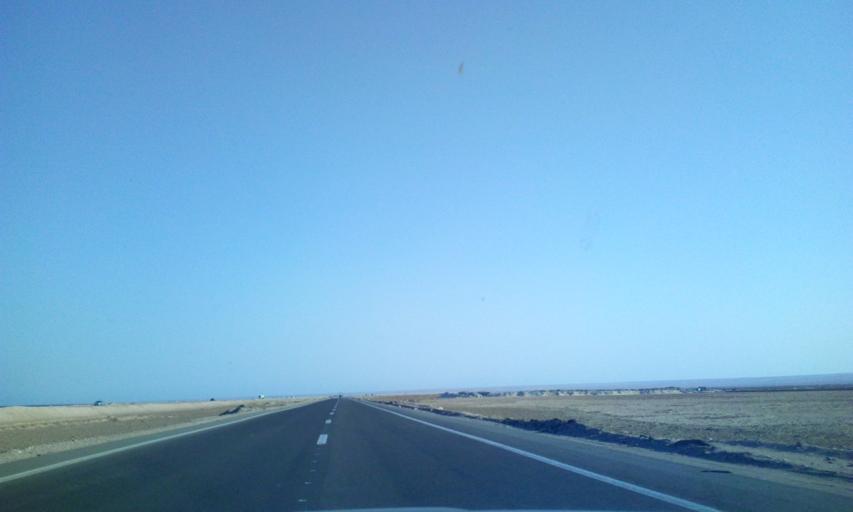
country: EG
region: South Sinai
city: Tor
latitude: 28.6326
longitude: 32.8573
